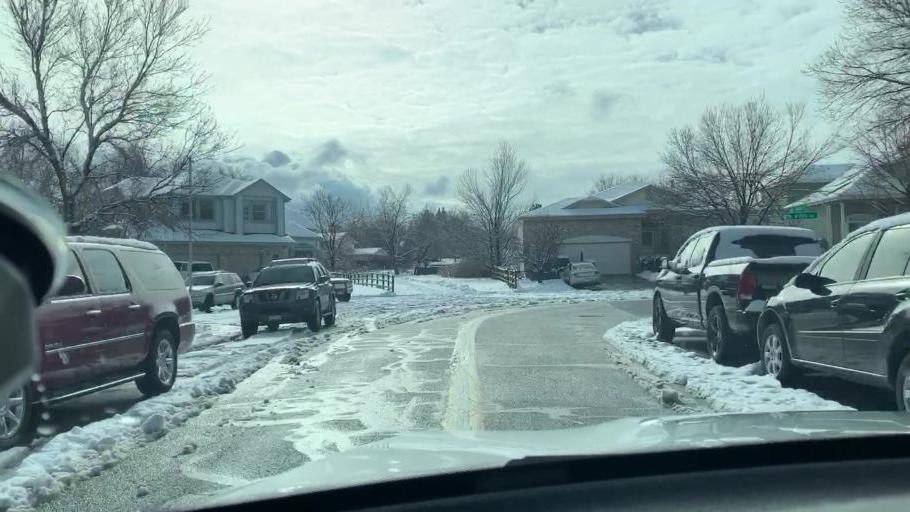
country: US
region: Colorado
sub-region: Adams County
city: Northglenn
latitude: 39.8987
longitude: -105.0003
